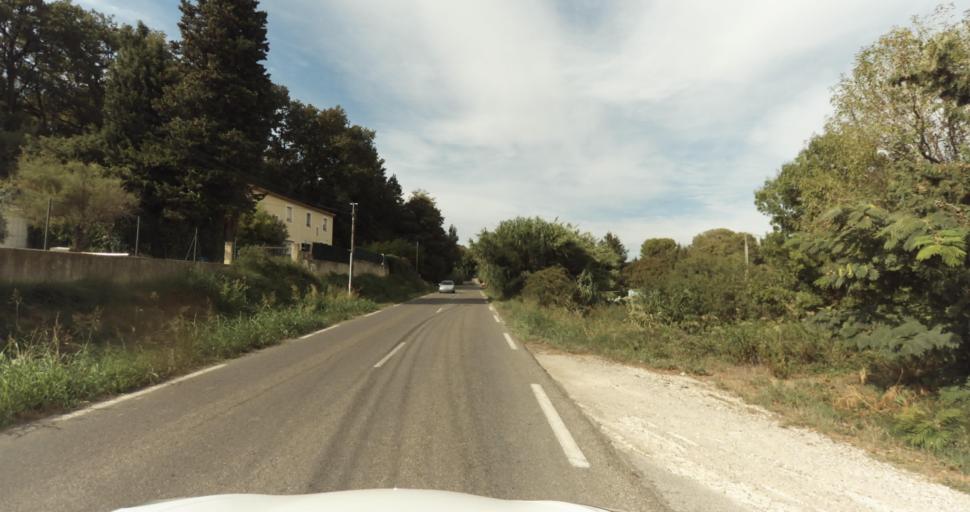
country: FR
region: Provence-Alpes-Cote d'Azur
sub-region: Departement des Bouches-du-Rhone
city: Miramas
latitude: 43.5661
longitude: 5.0154
